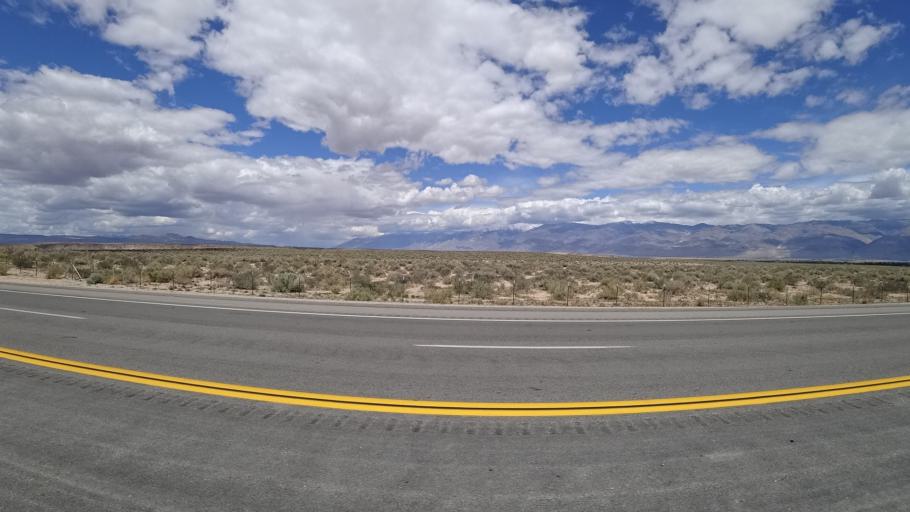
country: US
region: California
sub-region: Inyo County
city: West Bishop
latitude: 37.3778
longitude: -118.4696
